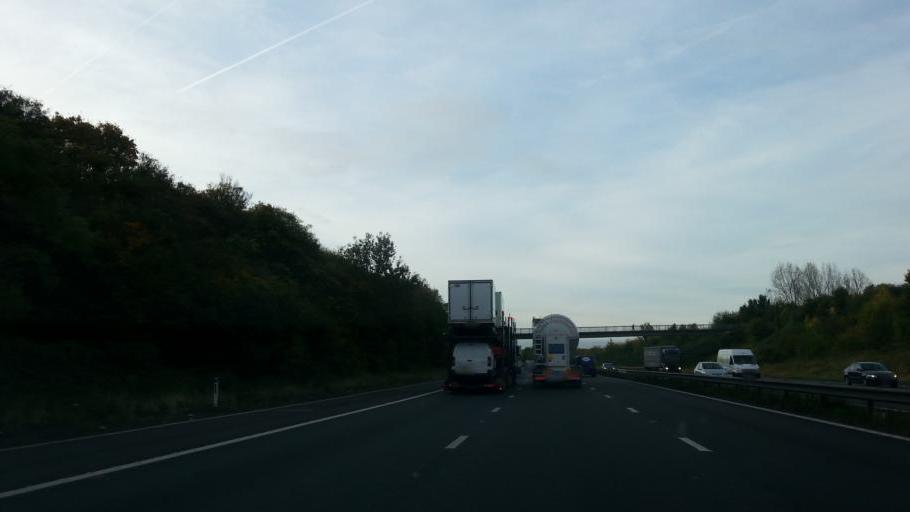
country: GB
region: England
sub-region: Leicestershire
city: Enderby
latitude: 52.5834
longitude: -1.1981
